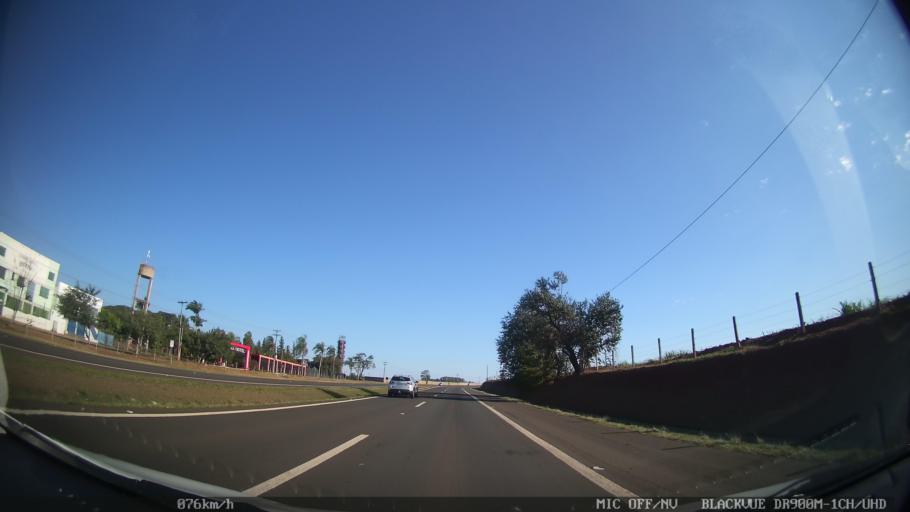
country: BR
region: Sao Paulo
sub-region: Piracicaba
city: Piracicaba
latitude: -22.6864
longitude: -47.6399
